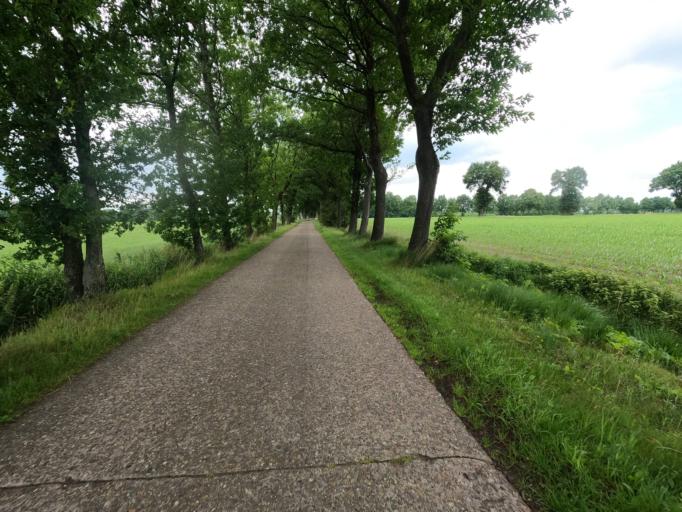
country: BE
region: Flanders
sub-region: Provincie Antwerpen
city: Kalmthout
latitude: 51.4210
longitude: 4.5129
